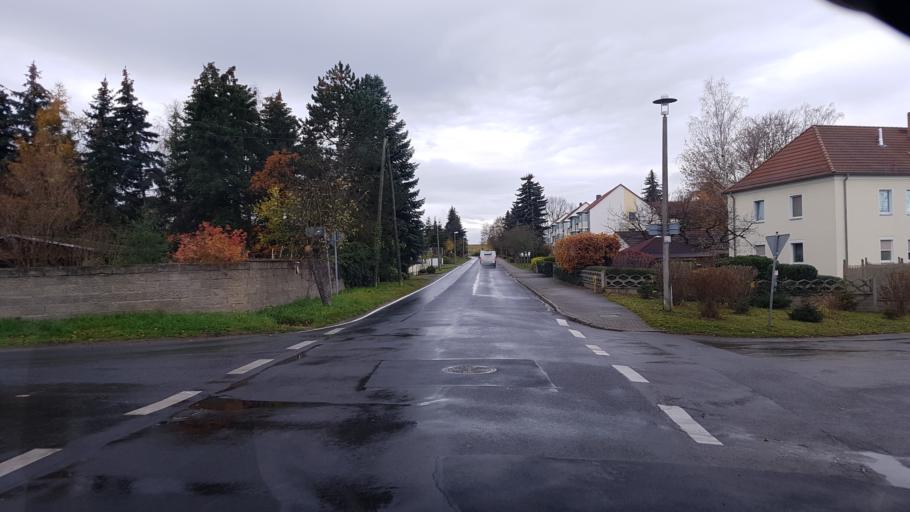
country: DE
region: Brandenburg
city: Ortrand
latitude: 51.3719
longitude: 13.7559
